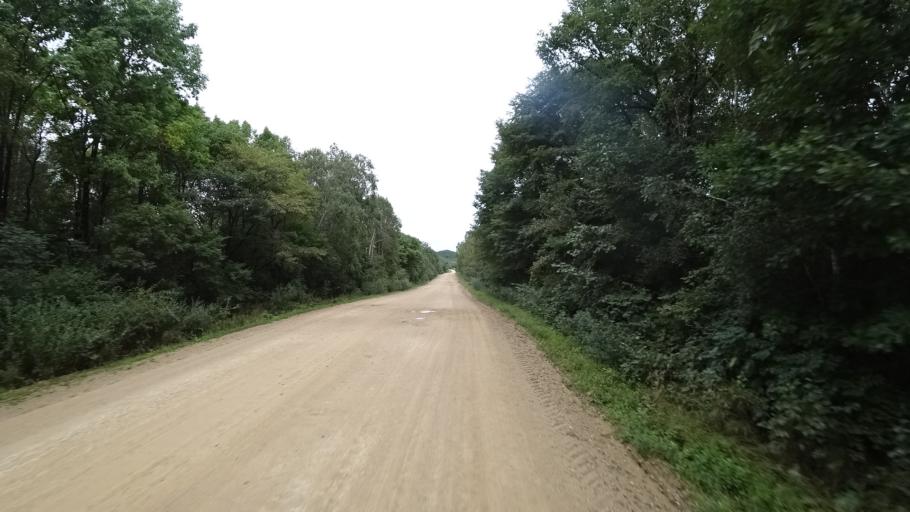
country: RU
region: Primorskiy
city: Rettikhovka
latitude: 44.1625
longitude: 132.7287
